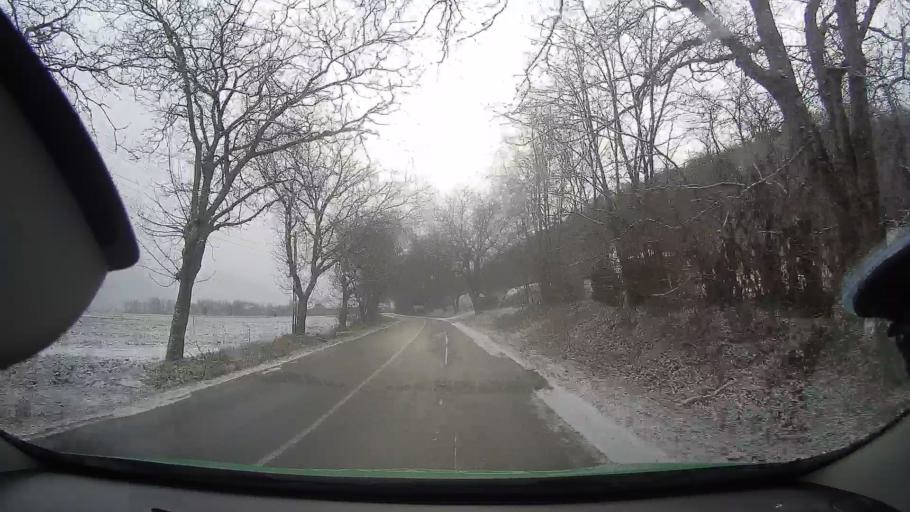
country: RO
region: Alba
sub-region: Comuna Rimetea
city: Rimetea
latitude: 46.4281
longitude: 23.5611
